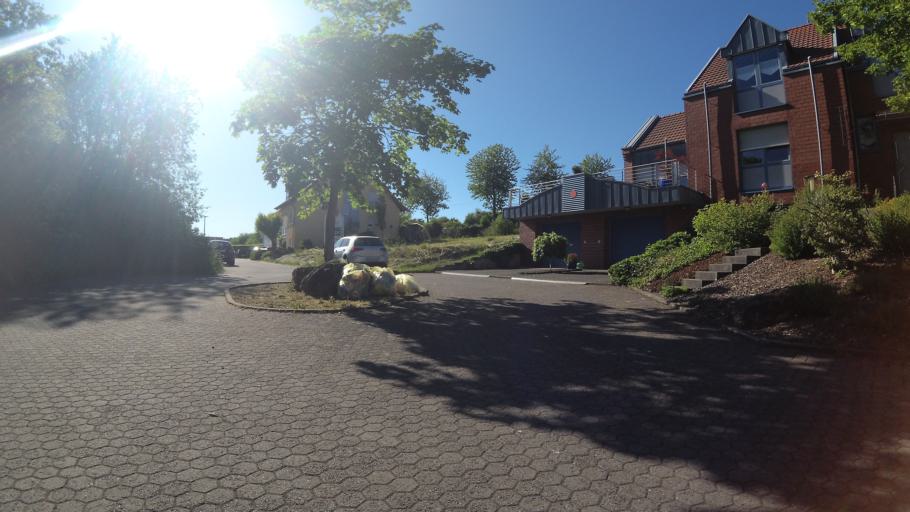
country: DE
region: Saarland
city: Marpingen
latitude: 49.4487
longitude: 7.0466
